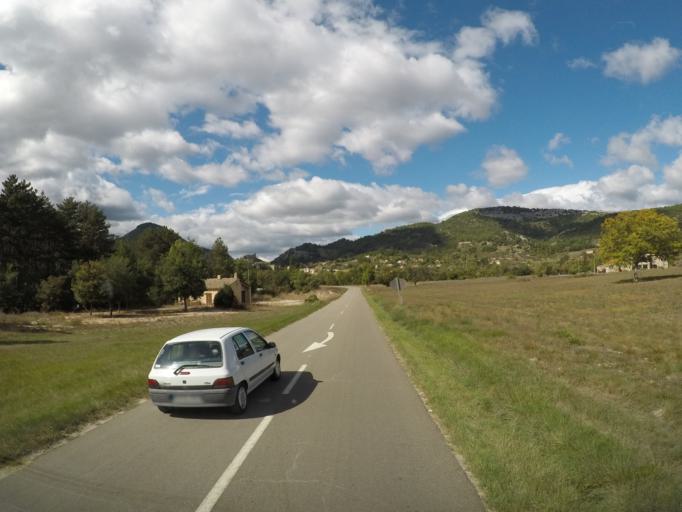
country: FR
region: Provence-Alpes-Cote d'Azur
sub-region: Departement du Vaucluse
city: Sault
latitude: 44.1655
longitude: 5.4300
